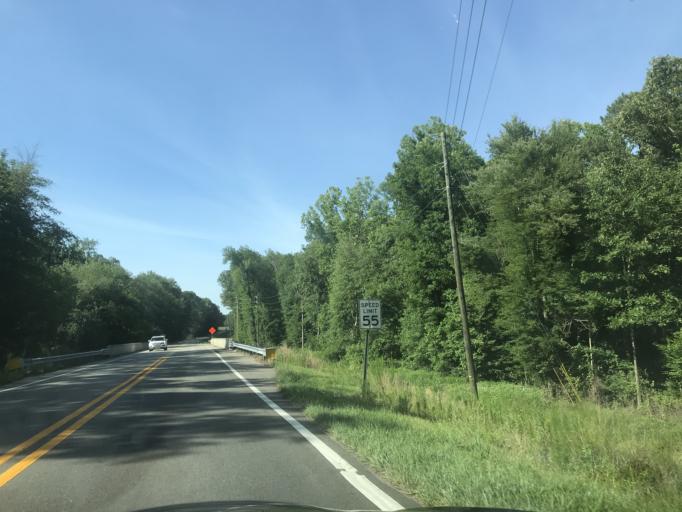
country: US
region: North Carolina
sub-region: Johnston County
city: Clayton
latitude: 35.5993
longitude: -78.5358
